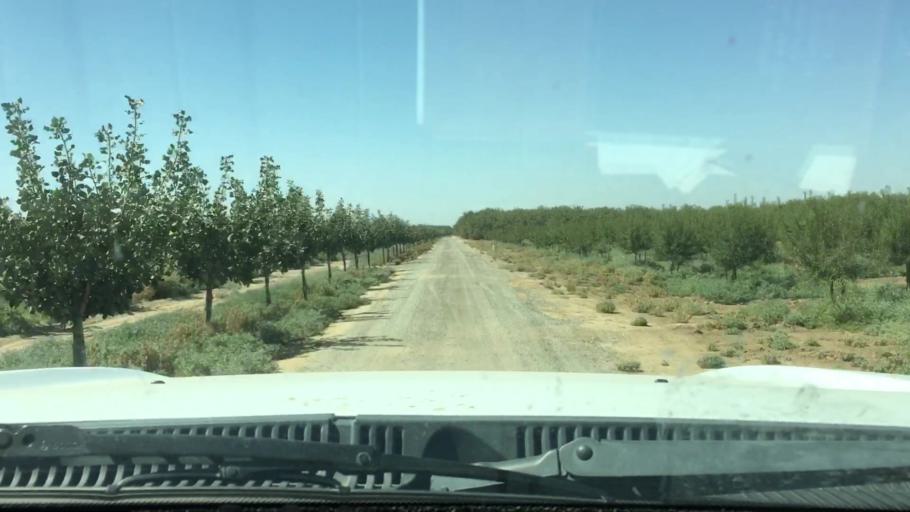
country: US
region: California
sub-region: Kern County
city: Shafter
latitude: 35.4527
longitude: -119.2901
